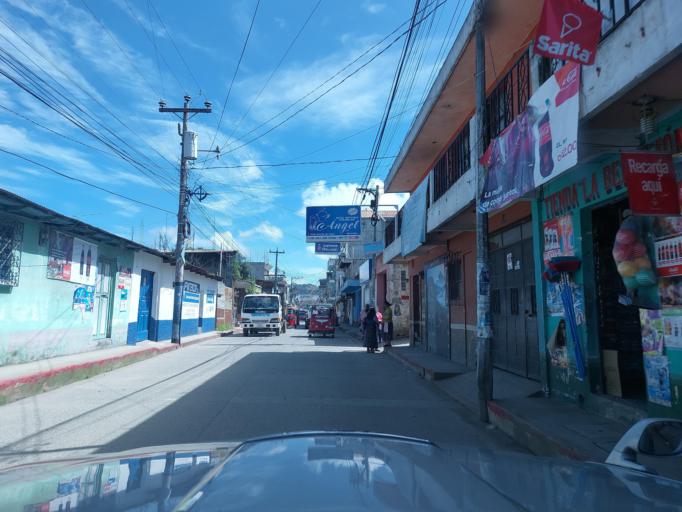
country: GT
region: Chimaltenango
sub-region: Municipio de San Juan Comalapa
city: Comalapa
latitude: 14.7362
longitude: -90.8871
